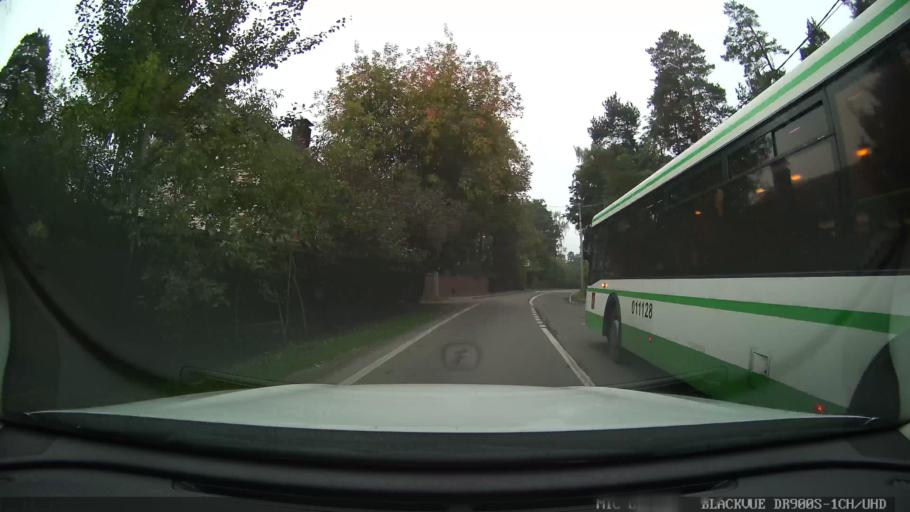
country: RU
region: Moscow
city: Novo-Peredelkino
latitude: 55.6533
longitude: 37.3554
